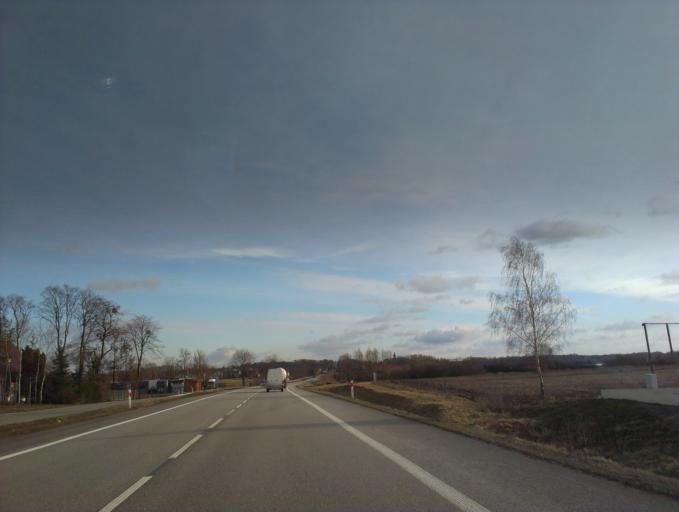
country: PL
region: Kujawsko-Pomorskie
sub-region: Powiat lipnowski
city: Kikol
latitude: 52.9177
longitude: 19.1025
